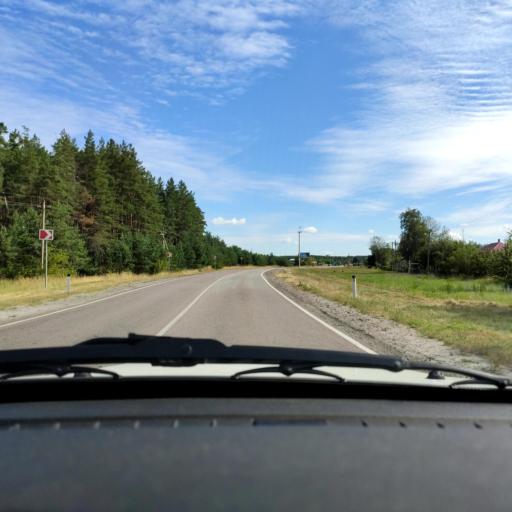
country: RU
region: Voronezj
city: Uglyanets
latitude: 51.8512
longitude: 39.6606
